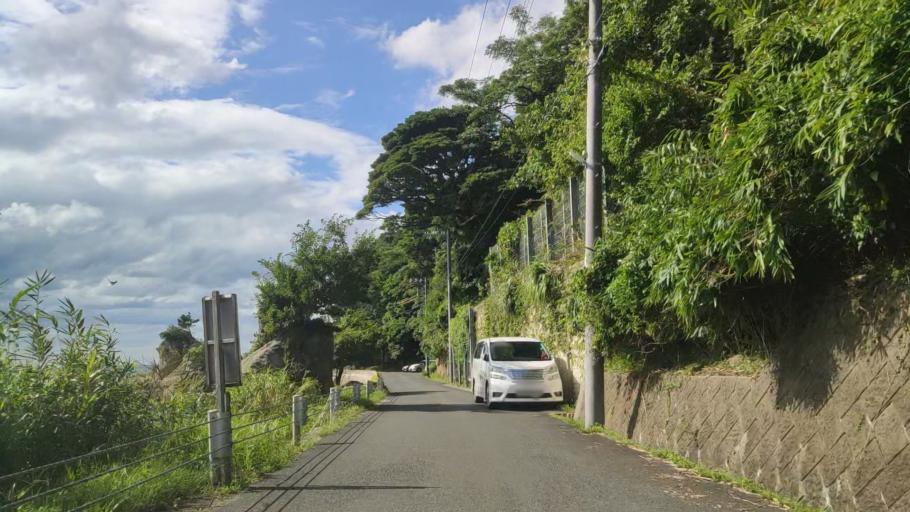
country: JP
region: Hyogo
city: Toyooka
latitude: 35.6703
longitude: 134.9662
